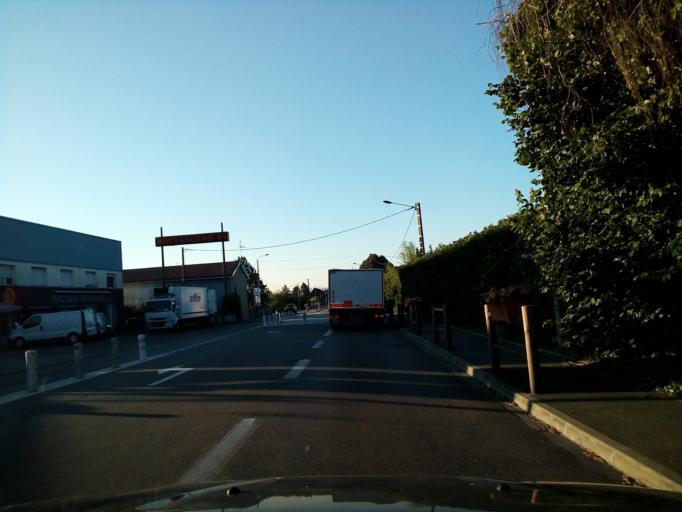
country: FR
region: Rhone-Alpes
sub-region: Departement de l'Isere
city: La Verpilliere
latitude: 45.6435
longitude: 5.1335
